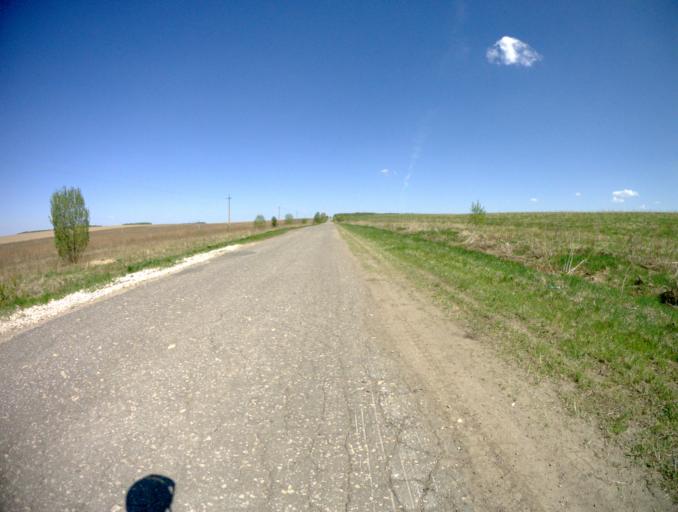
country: RU
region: Vladimir
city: Suzdal'
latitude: 56.3018
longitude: 40.3720
